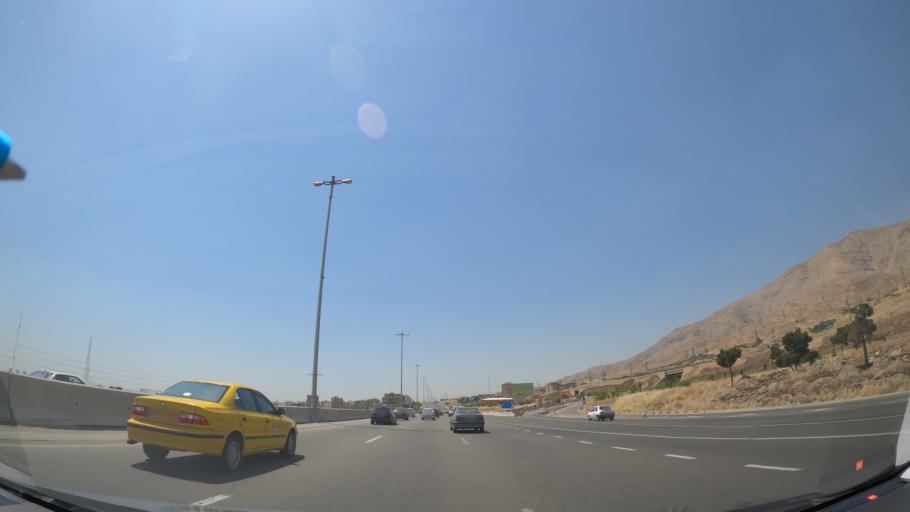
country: IR
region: Tehran
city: Shahr-e Qods
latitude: 35.7518
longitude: 51.0786
